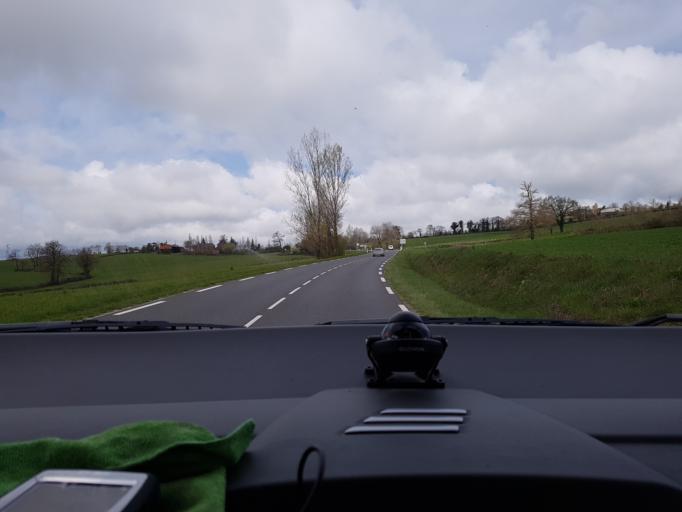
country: FR
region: Midi-Pyrenees
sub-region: Departement de l'Aveyron
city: Colombies
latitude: 44.3973
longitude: 2.3695
